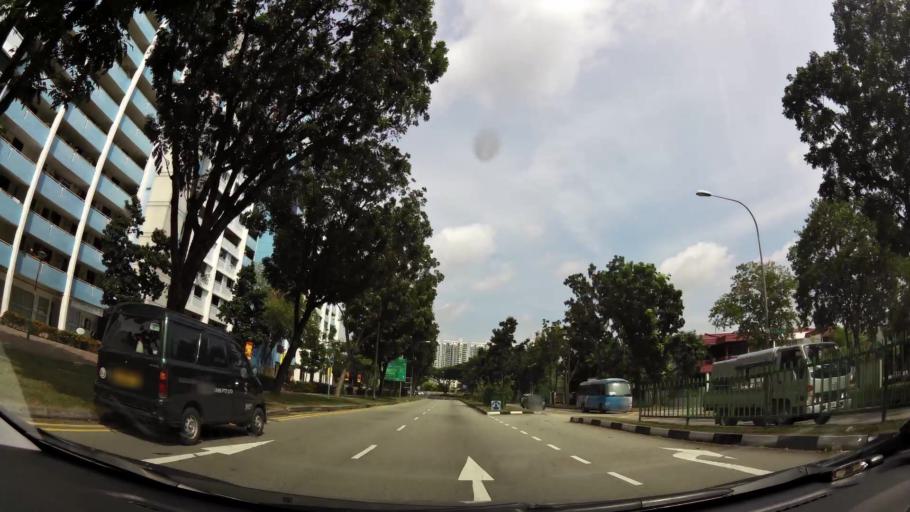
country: SG
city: Singapore
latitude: 1.3050
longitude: 103.7642
